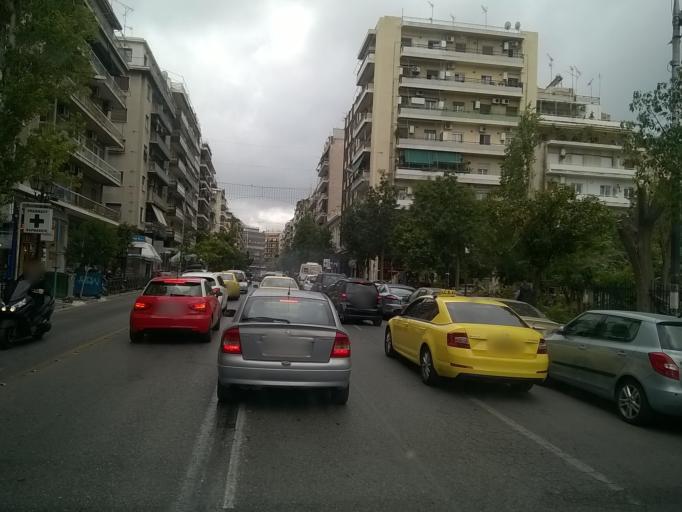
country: GR
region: Attica
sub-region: Nomos Attikis
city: Piraeus
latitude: 37.9388
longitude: 23.6434
